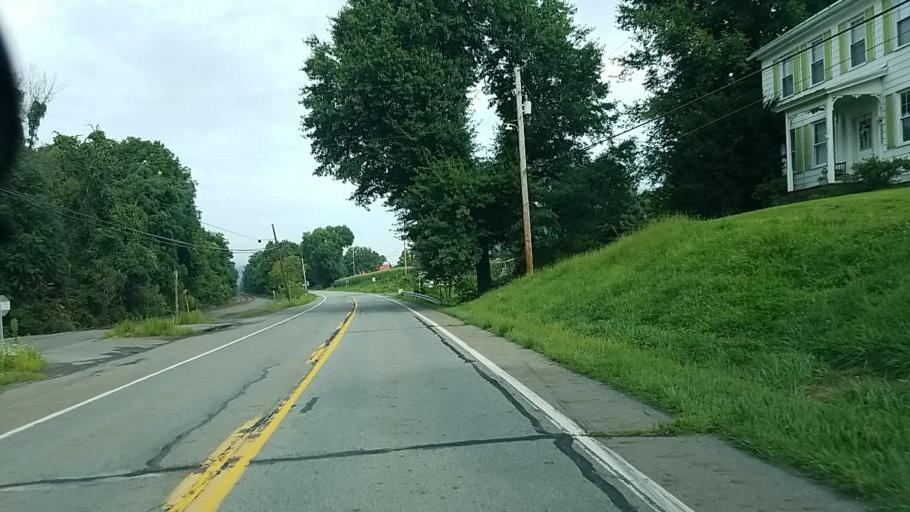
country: US
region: Pennsylvania
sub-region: Dauphin County
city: Millersburg
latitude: 40.5008
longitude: -76.9469
